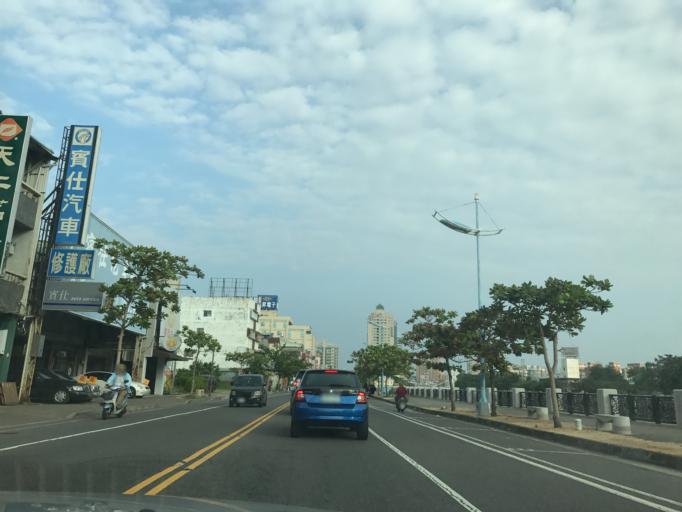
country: TW
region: Taiwan
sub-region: Tainan
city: Tainan
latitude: 22.9983
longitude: 120.1824
